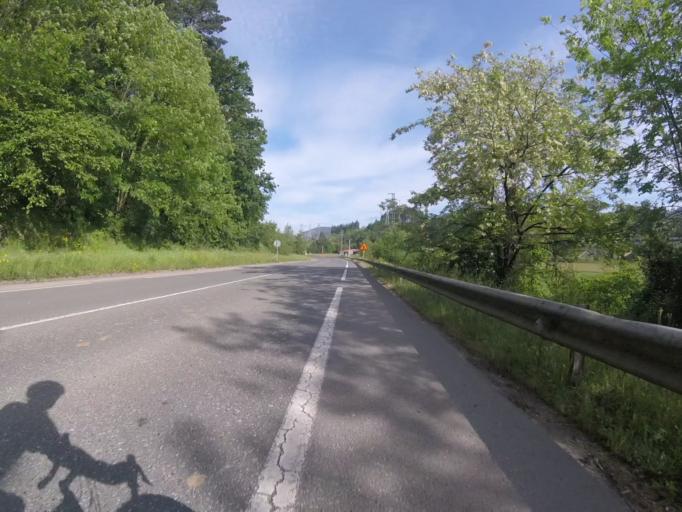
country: ES
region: Basque Country
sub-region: Provincia de Guipuzcoa
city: Gabiria
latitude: 43.0583
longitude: -2.2684
